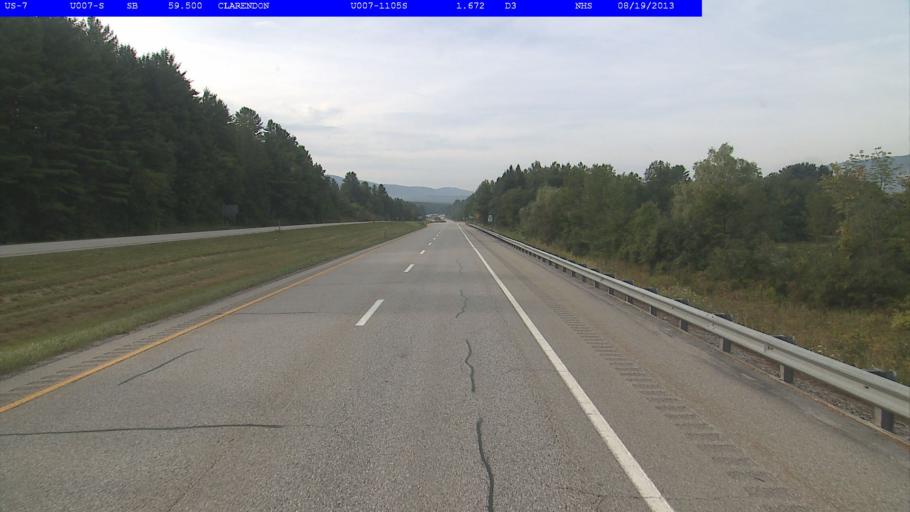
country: US
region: Vermont
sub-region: Rutland County
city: Rutland
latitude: 43.5190
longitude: -72.9679
